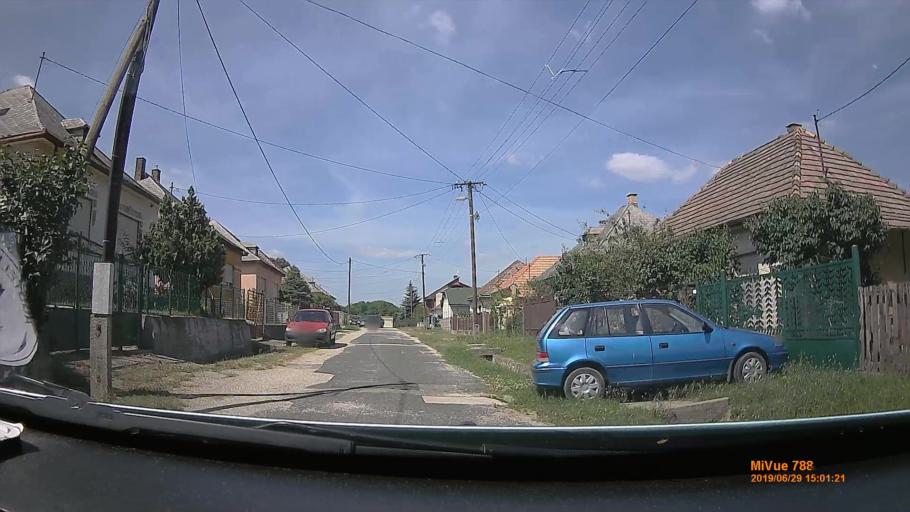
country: HU
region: Komarom-Esztergom
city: Nyergesujfalu
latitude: 47.7205
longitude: 18.5597
